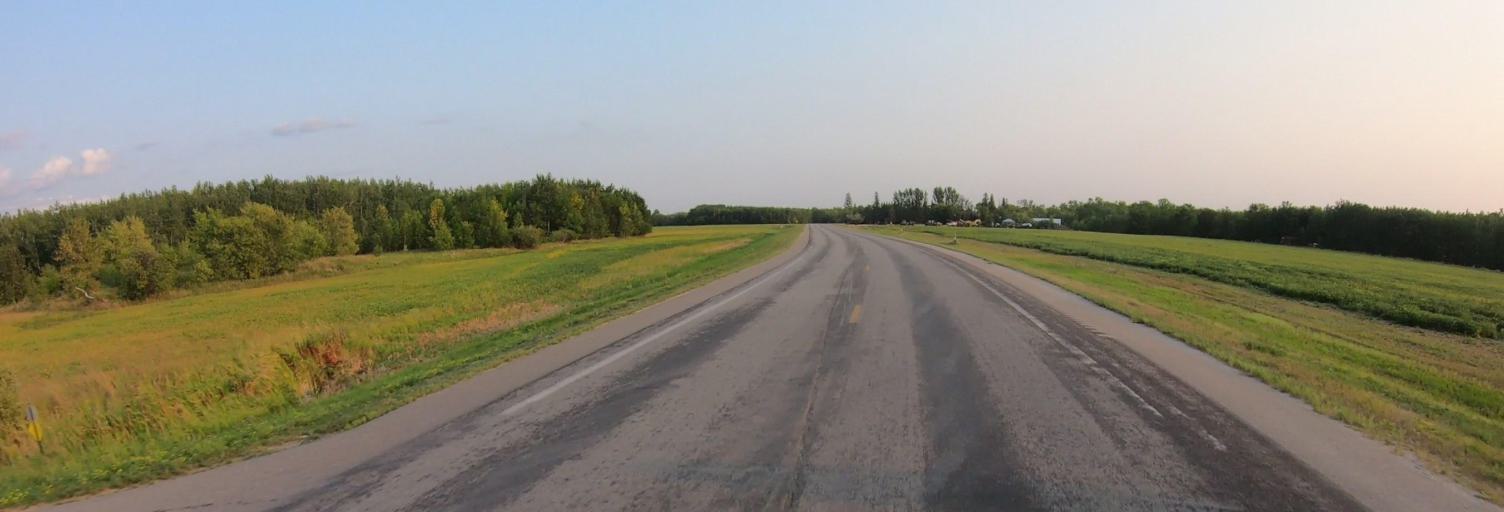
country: US
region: Minnesota
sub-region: Roseau County
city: Warroad
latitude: 48.8870
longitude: -95.3202
